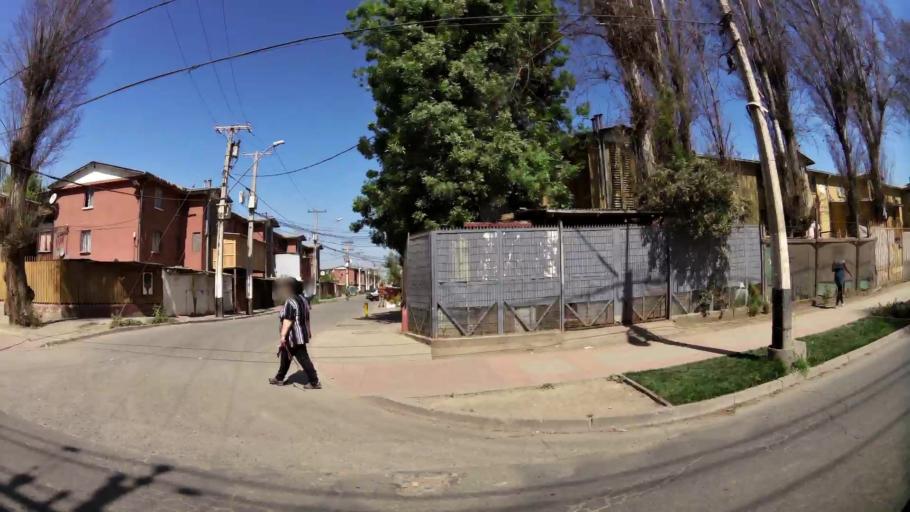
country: CL
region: Santiago Metropolitan
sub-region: Provincia de Santiago
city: Lo Prado
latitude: -33.3647
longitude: -70.7501
